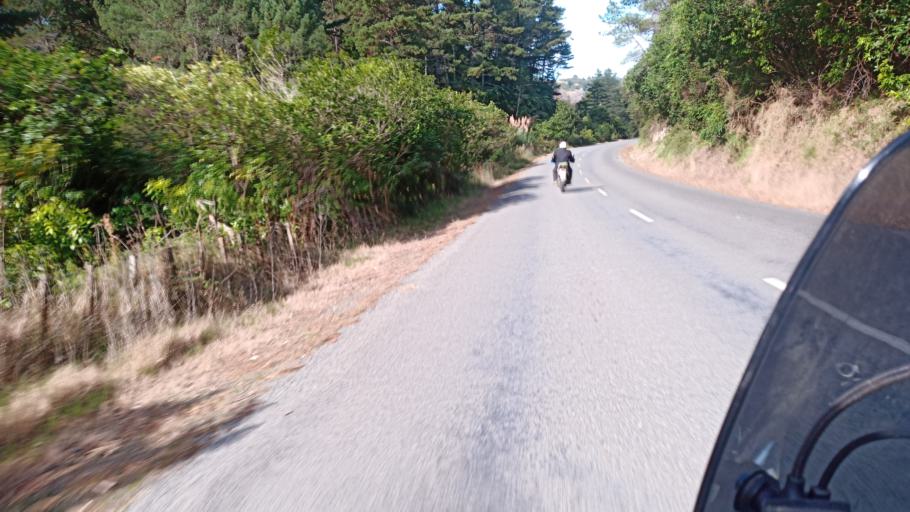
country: NZ
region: Hawke's Bay
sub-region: Wairoa District
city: Wairoa
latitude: -39.0370
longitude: 177.1051
